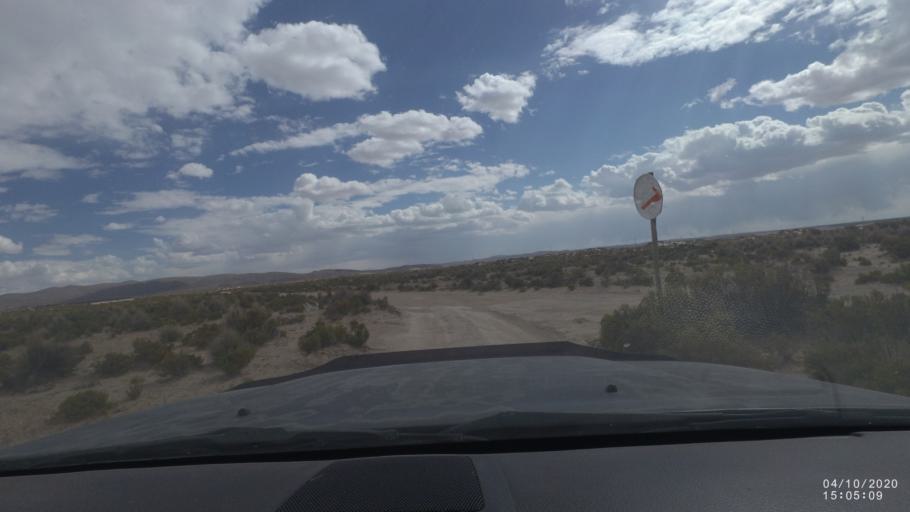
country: BO
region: Oruro
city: Poopo
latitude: -18.6916
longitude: -67.5542
